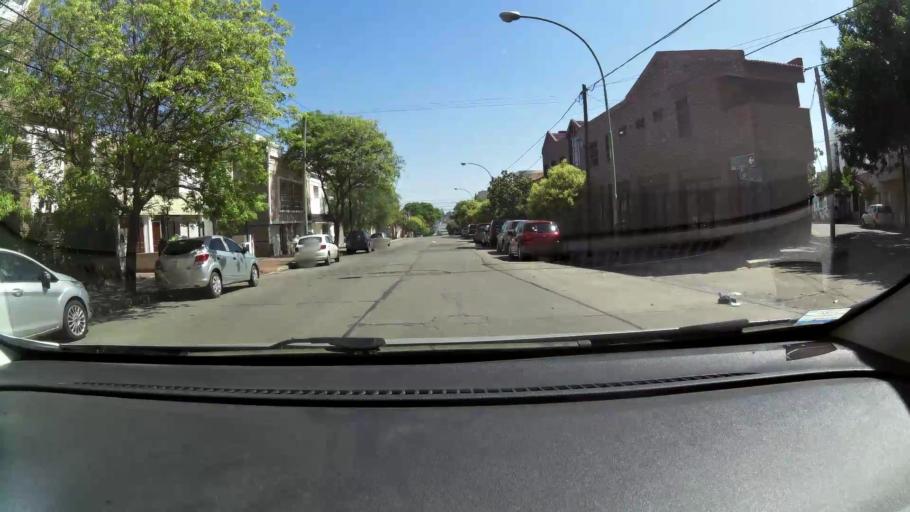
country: AR
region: Cordoba
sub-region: Departamento de Capital
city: Cordoba
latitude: -31.4019
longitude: -64.1794
